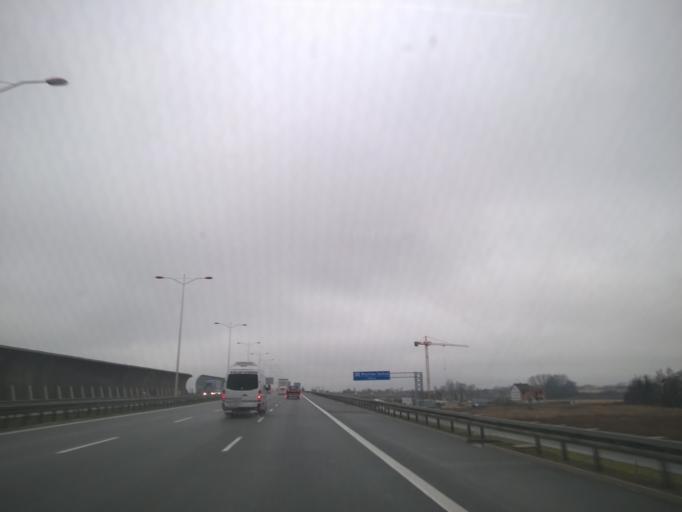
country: PL
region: Lower Silesian Voivodeship
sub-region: Powiat wroclawski
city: Smolec
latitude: 51.0999
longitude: 16.9331
